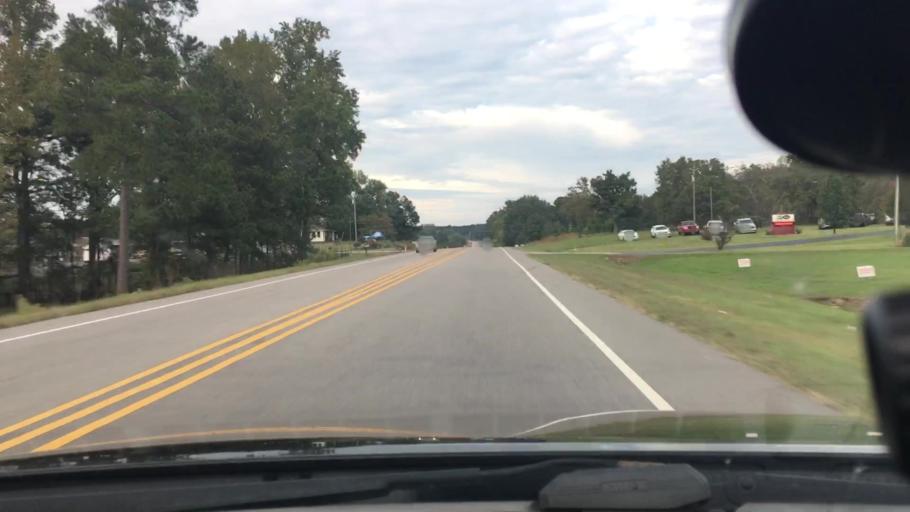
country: US
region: North Carolina
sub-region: Lee County
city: Sanford
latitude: 35.3949
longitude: -79.2435
